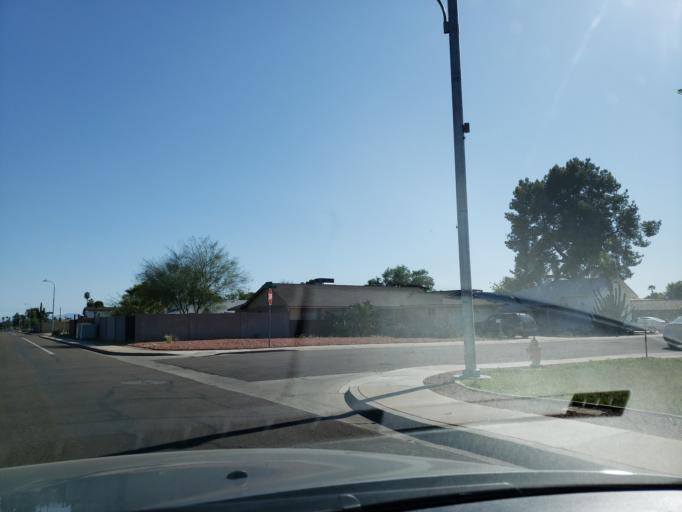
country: US
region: Arizona
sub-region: Maricopa County
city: Glendale
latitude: 33.5718
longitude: -112.1776
